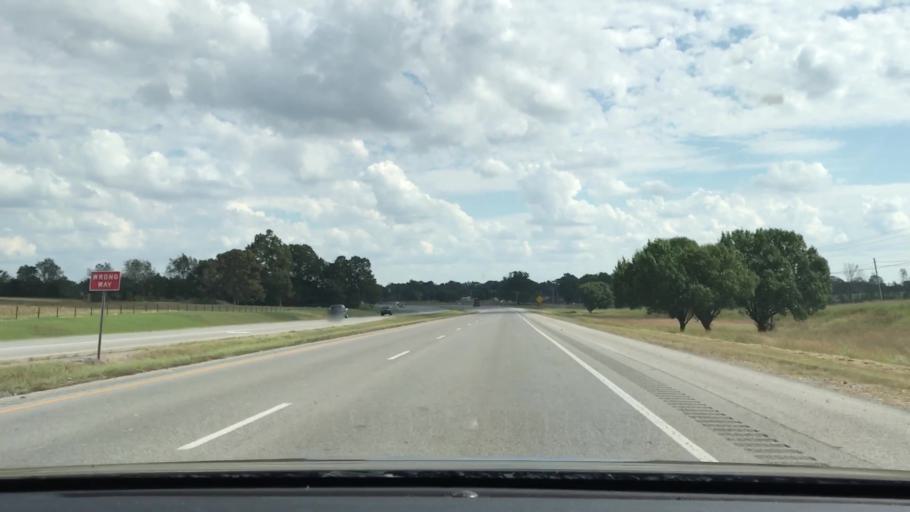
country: US
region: Kentucky
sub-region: Trigg County
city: Cadiz
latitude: 36.8675
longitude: -87.7834
